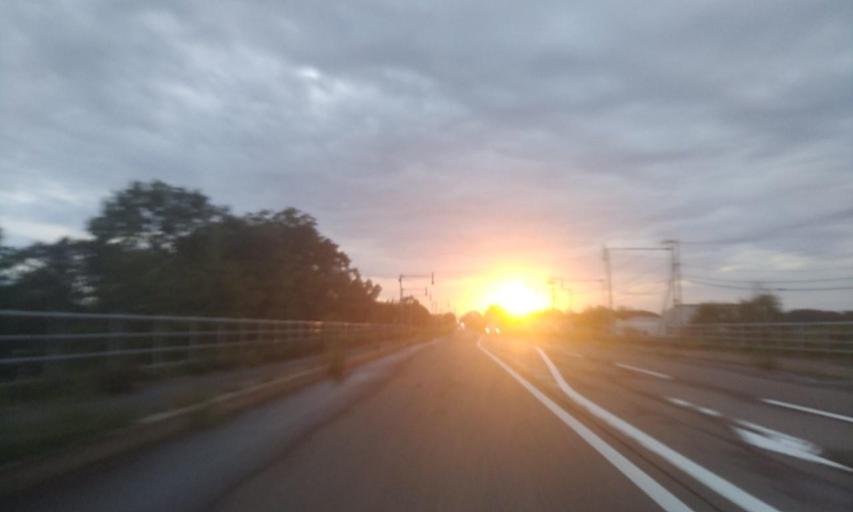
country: JP
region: Hokkaido
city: Abashiri
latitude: 43.8997
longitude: 144.6389
